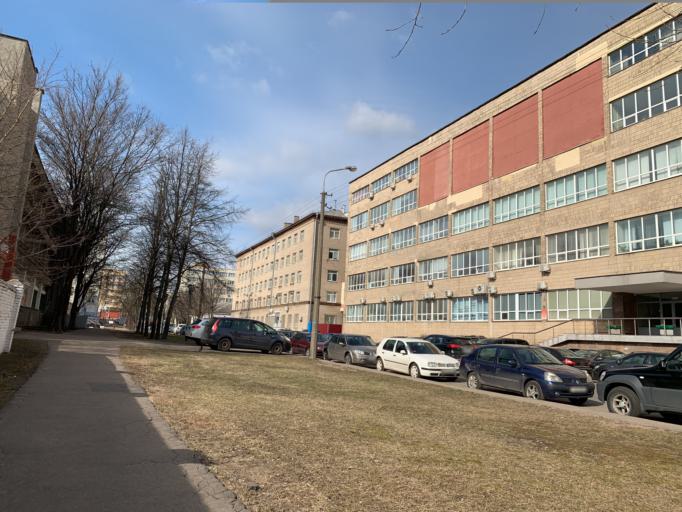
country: BY
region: Minsk
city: Minsk
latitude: 53.9111
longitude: 27.6033
